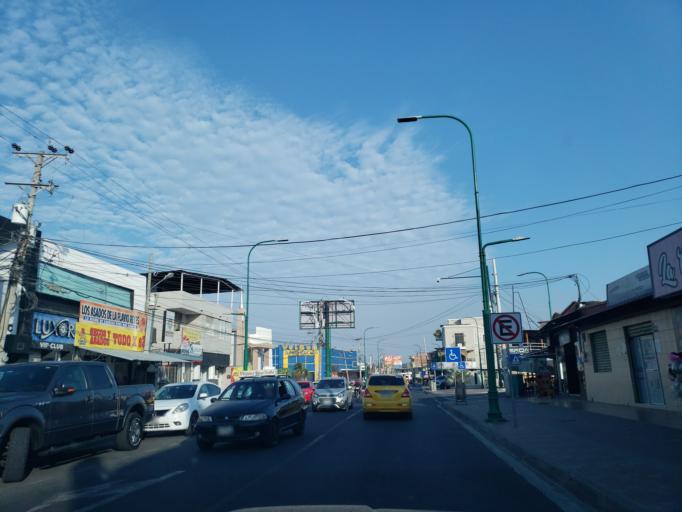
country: EC
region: Manabi
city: Manta
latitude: -0.9449
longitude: -80.7317
